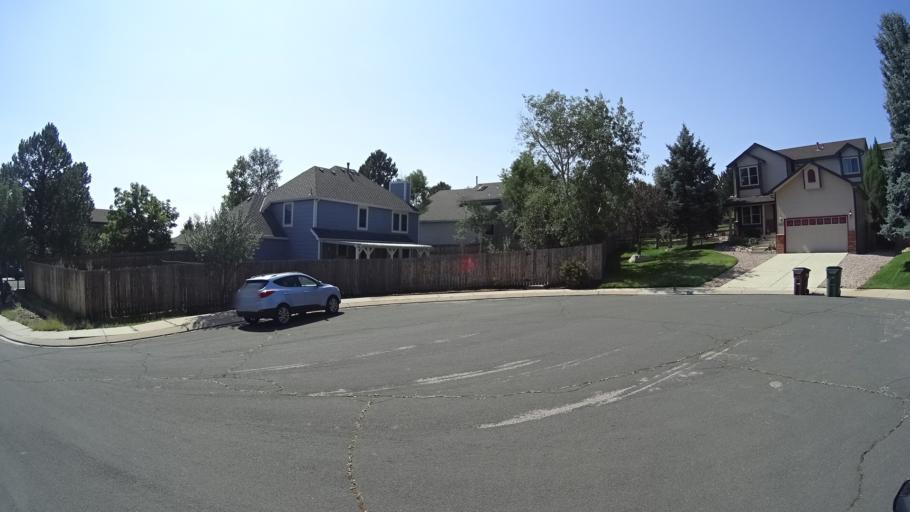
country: US
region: Colorado
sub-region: El Paso County
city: Air Force Academy
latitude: 38.9230
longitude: -104.8686
